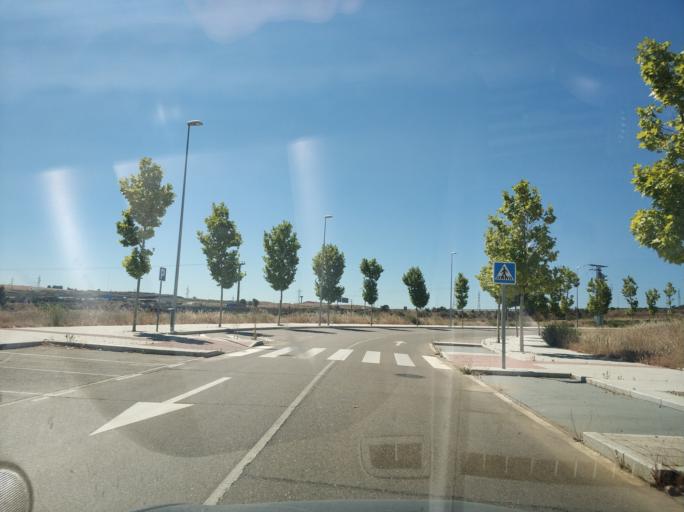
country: ES
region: Castille and Leon
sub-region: Provincia de Salamanca
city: Salamanca
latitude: 40.9599
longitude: -5.6989
